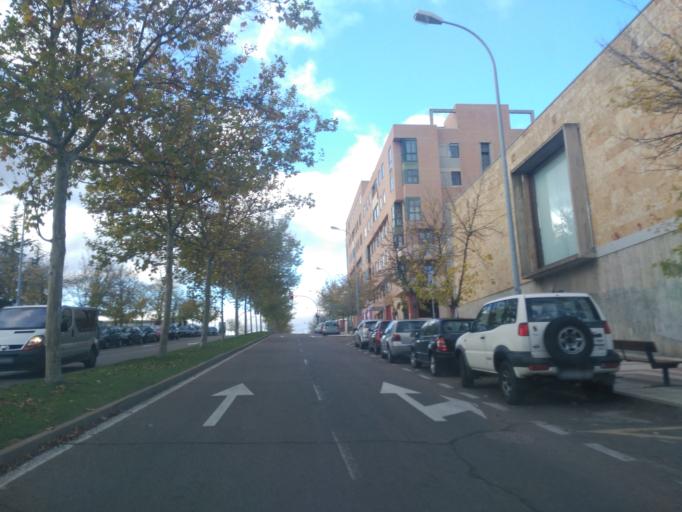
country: ES
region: Castille and Leon
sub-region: Provincia de Salamanca
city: Salamanca
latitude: 40.9779
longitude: -5.6550
